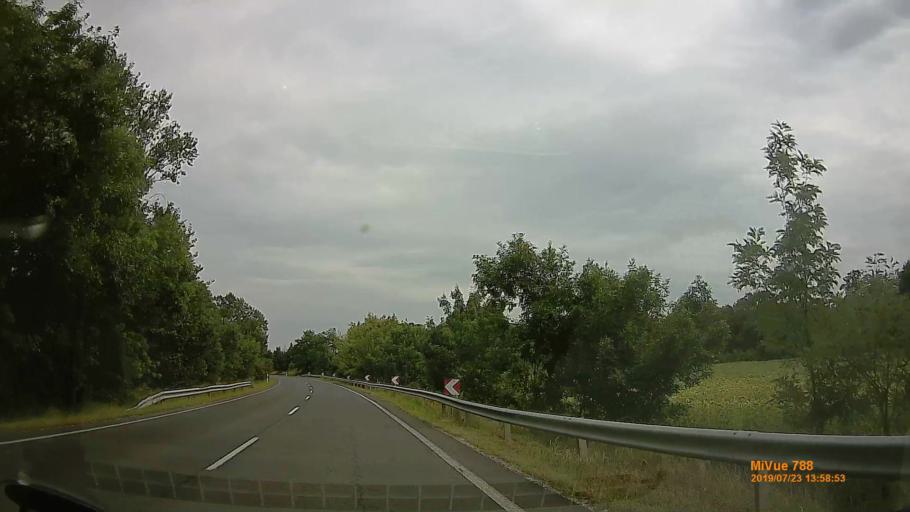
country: HU
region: Szabolcs-Szatmar-Bereg
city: Tiszavasvari
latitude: 47.9257
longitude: 21.2828
